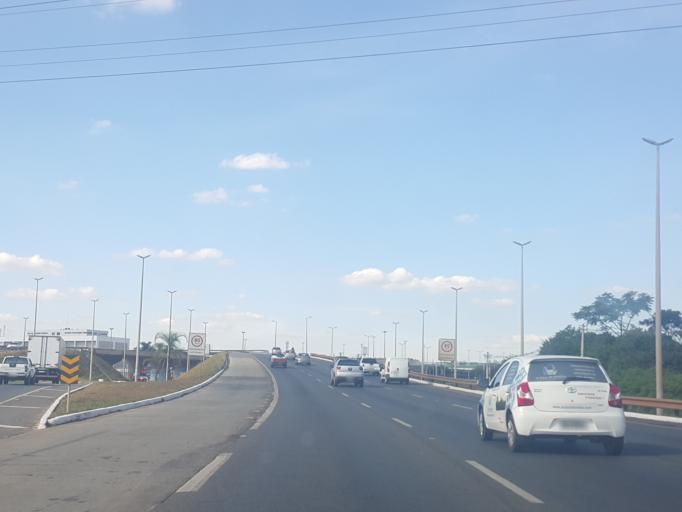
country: BR
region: Federal District
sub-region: Brasilia
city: Brasilia
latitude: -15.8084
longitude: -47.9709
